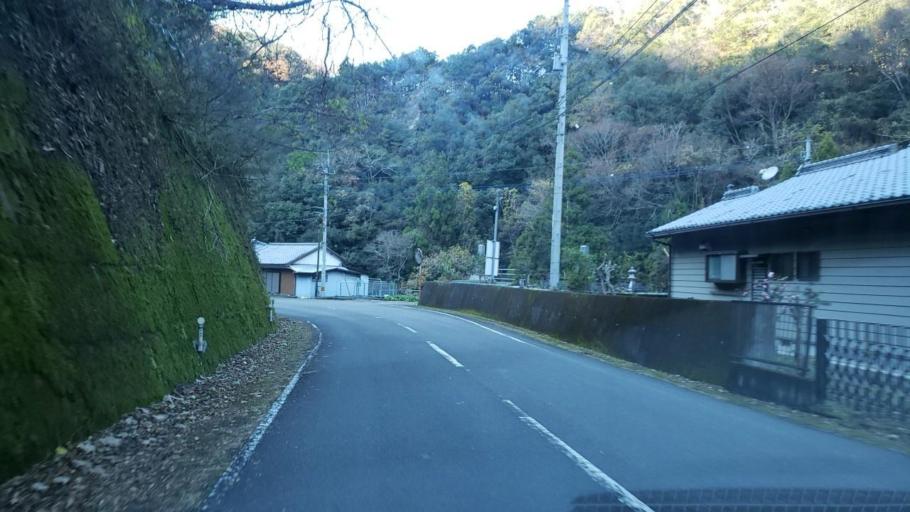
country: JP
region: Tokushima
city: Wakimachi
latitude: 34.0071
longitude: 134.0337
